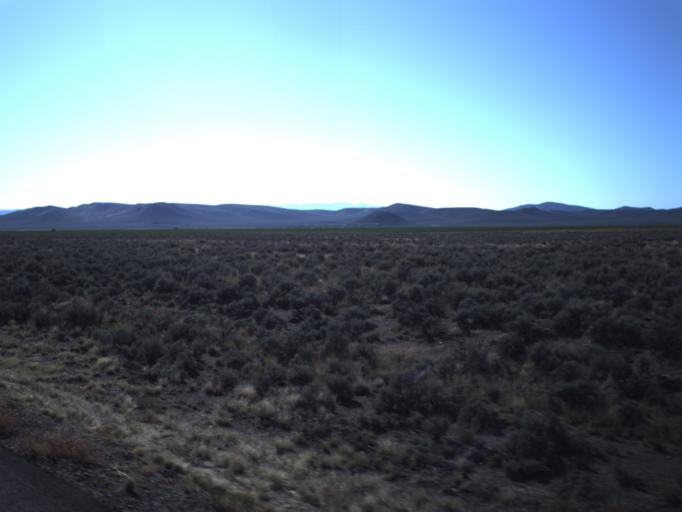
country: US
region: Utah
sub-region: Washington County
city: Enterprise
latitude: 37.7614
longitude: -113.8028
